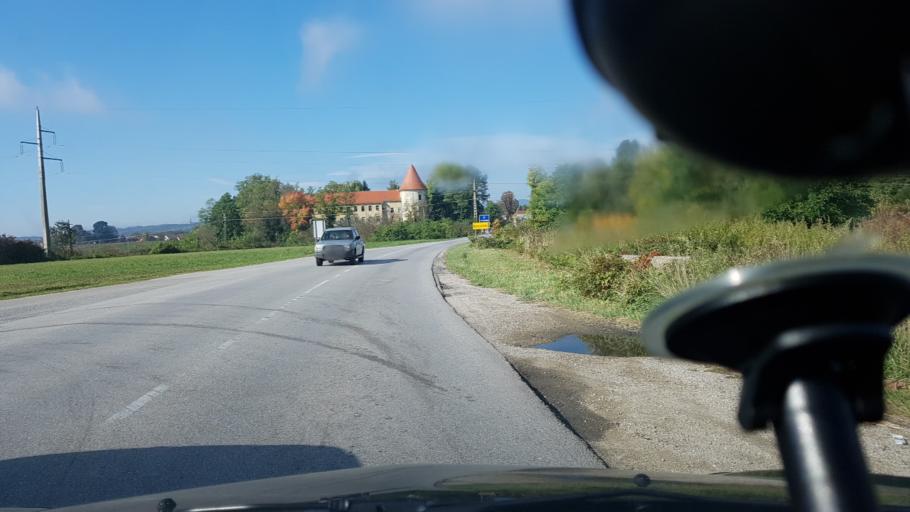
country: HR
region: Zagrebacka
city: Rakitje
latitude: 45.7750
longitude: 15.8207
